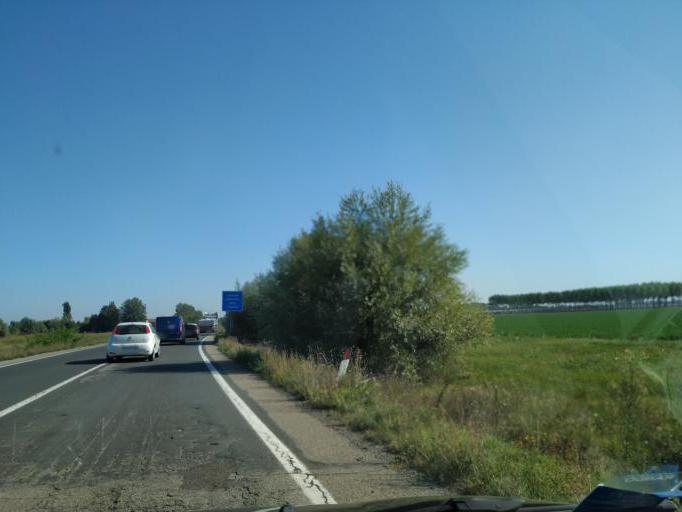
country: IT
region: Emilia-Romagna
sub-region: Provincia di Bologna
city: Decima
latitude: 44.7123
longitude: 11.2433
